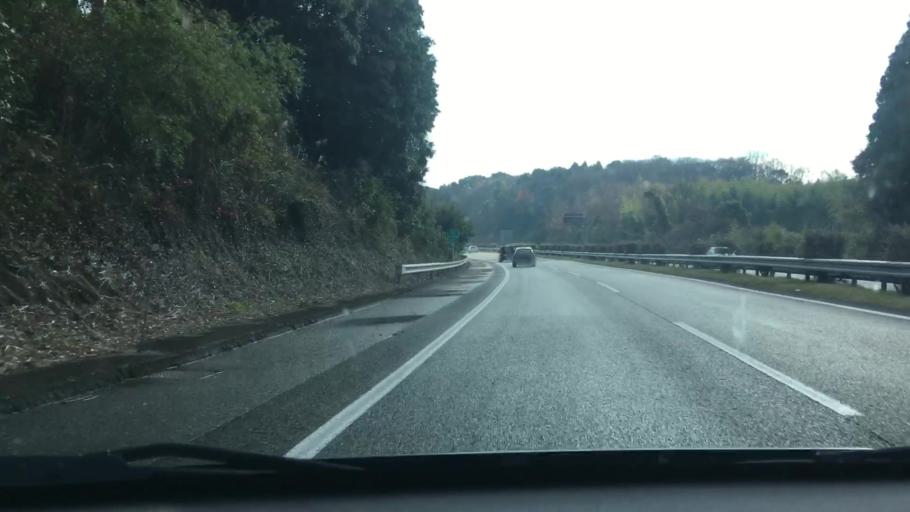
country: JP
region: Kumamoto
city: Matsubase
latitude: 32.6444
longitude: 130.7068
